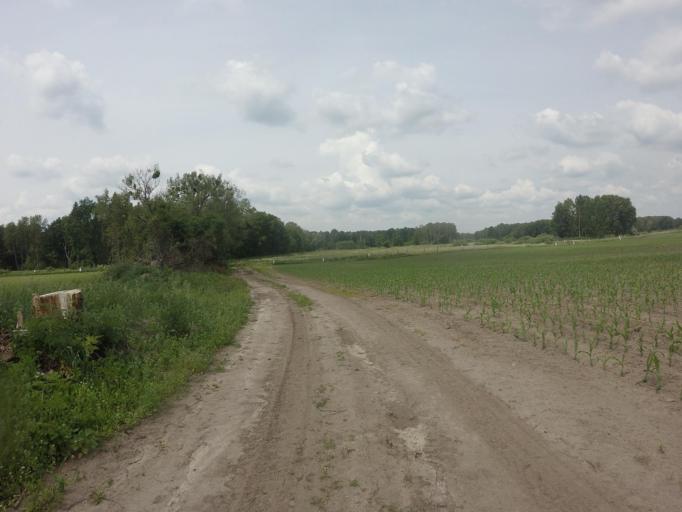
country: PL
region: West Pomeranian Voivodeship
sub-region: Powiat stargardzki
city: Dobrzany
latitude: 53.3002
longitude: 15.4760
